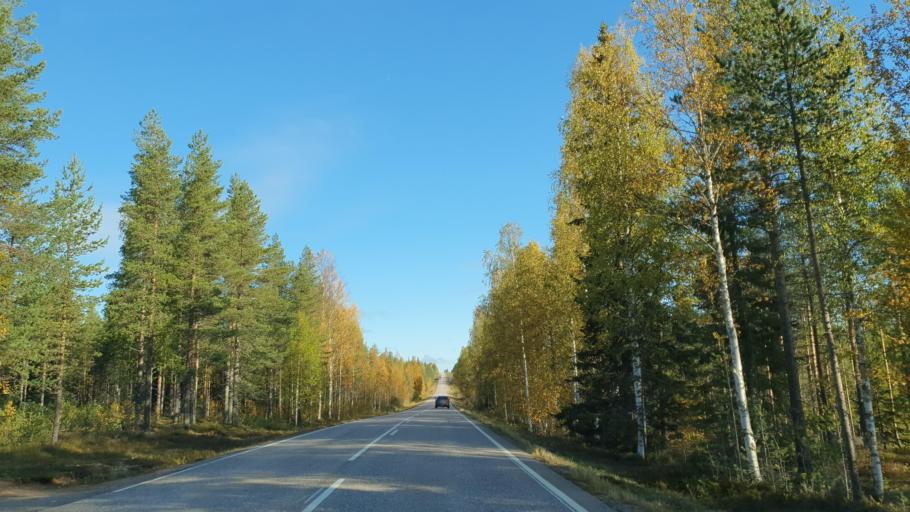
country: FI
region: Kainuu
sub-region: Kehys-Kainuu
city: Puolanka
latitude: 64.9368
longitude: 27.6025
